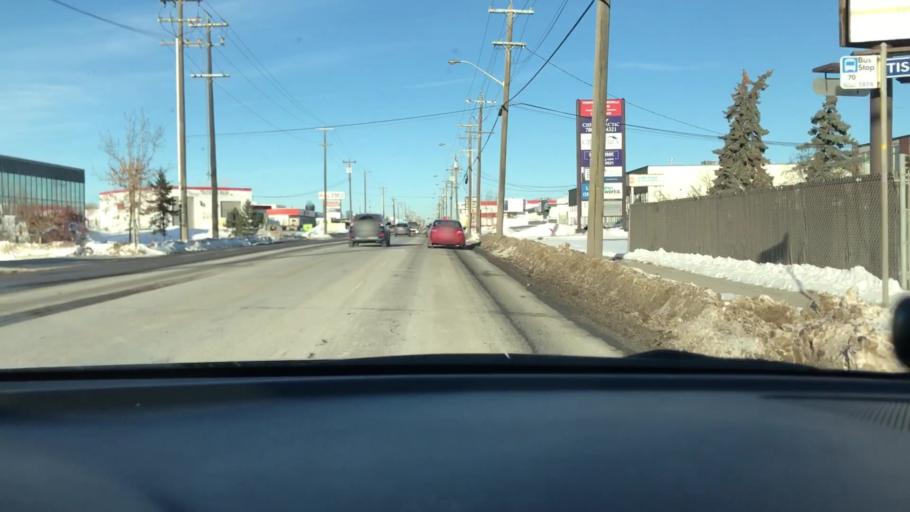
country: CA
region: Alberta
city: Edmonton
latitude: 53.4923
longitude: -113.4861
